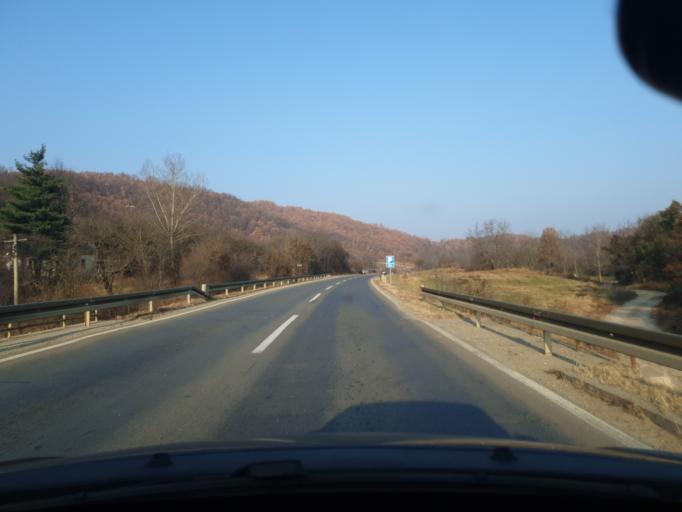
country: RS
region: Central Serbia
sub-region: Jablanicki Okrug
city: Vlasotince
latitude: 42.8968
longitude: 22.0485
